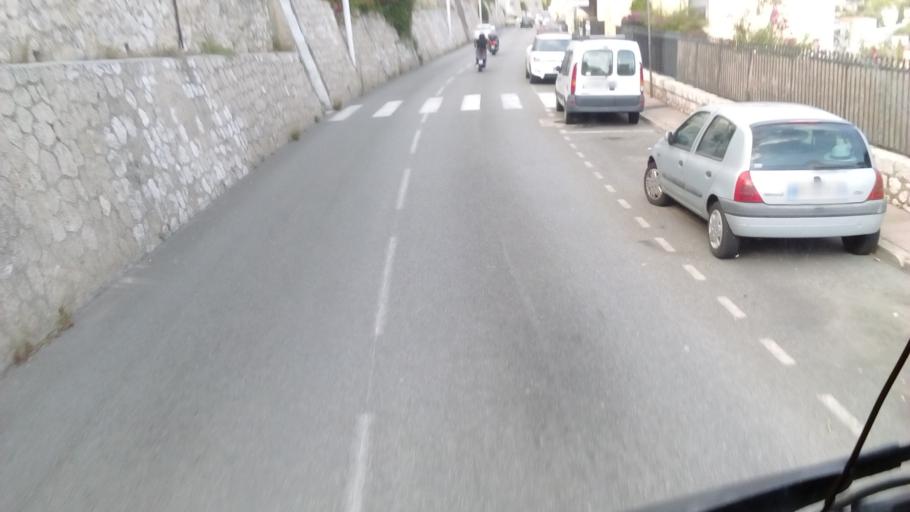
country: MC
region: Commune de Monaco
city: Saint-Roman
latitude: 43.7588
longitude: 7.4508
